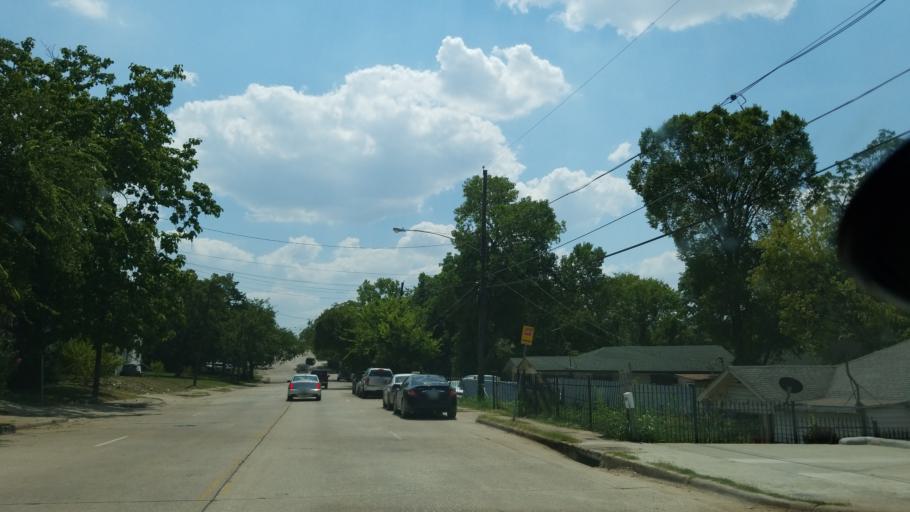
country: US
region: Texas
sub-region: Dallas County
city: Dallas
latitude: 32.7444
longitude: -96.7953
